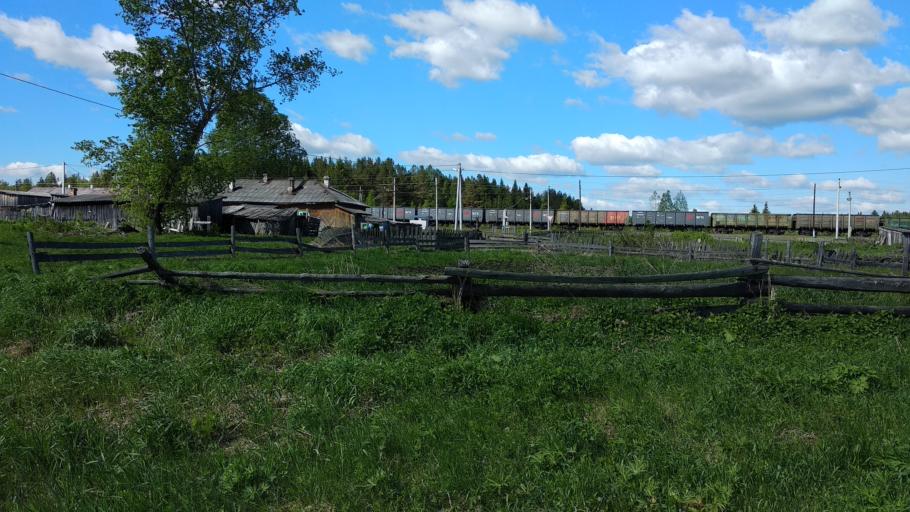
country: RU
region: Sverdlovsk
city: Volchansk
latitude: 60.2105
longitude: 60.4139
